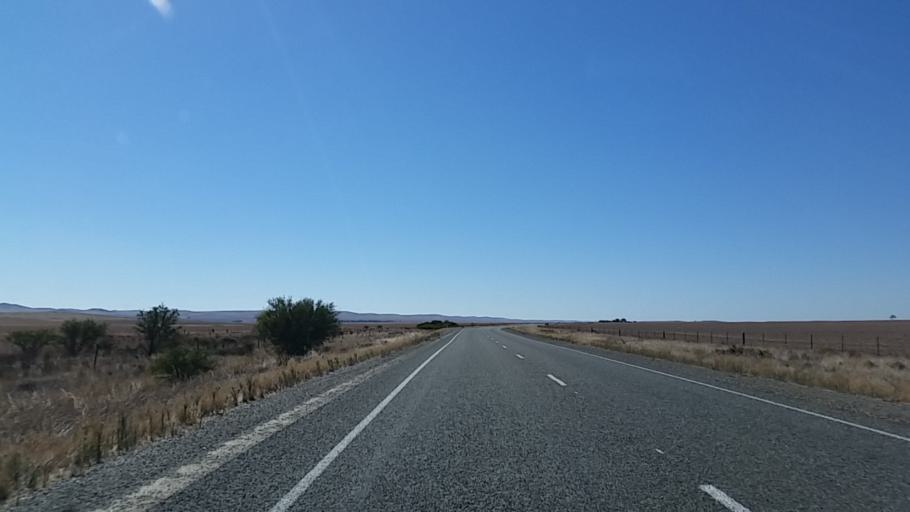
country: AU
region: South Australia
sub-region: Northern Areas
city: Jamestown
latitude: -33.2720
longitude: 138.8683
